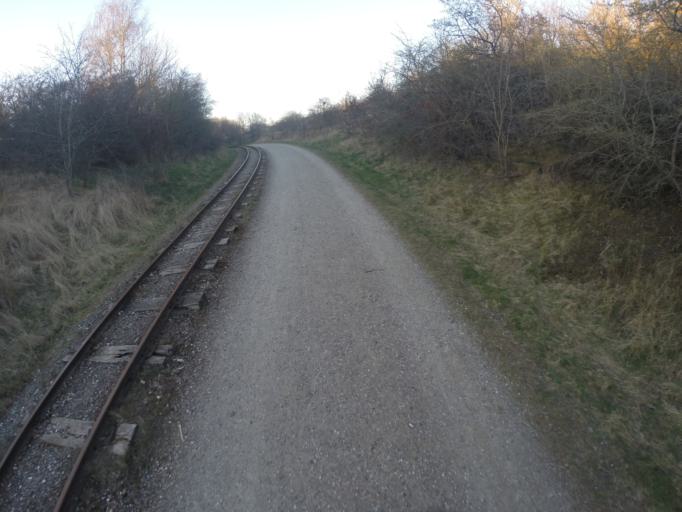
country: DK
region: Capital Region
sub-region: Hoje-Taastrup Kommune
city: Flong
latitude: 55.6395
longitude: 12.1876
